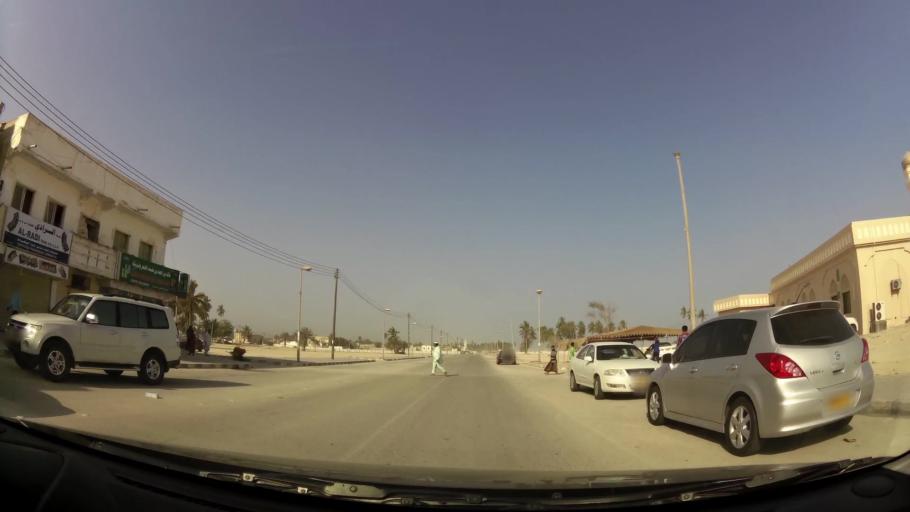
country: OM
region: Zufar
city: Salalah
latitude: 17.0006
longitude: 54.1028
